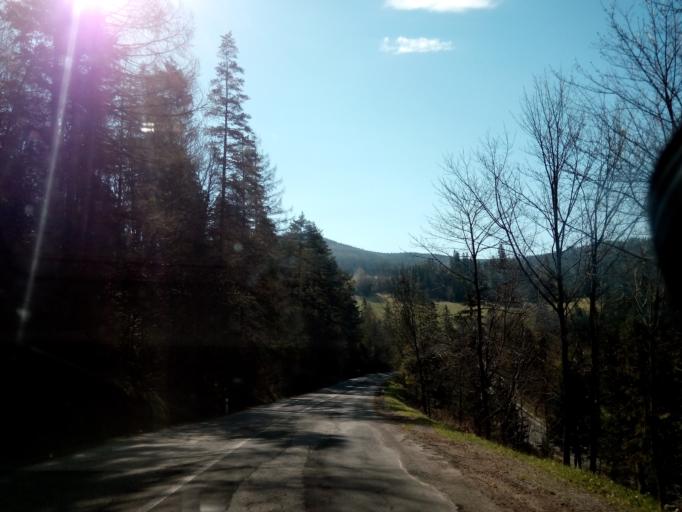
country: SK
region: Presovsky
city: Spisska Bela
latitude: 49.2933
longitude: 20.4107
